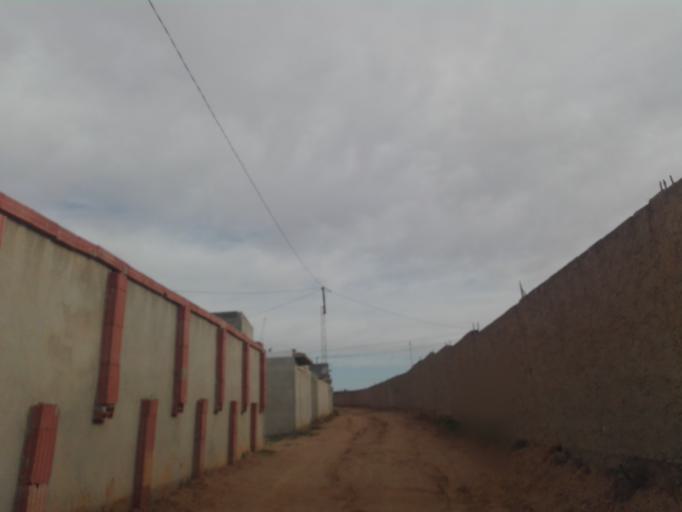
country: TN
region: Safaqis
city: Sfax
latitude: 34.7383
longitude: 10.5138
